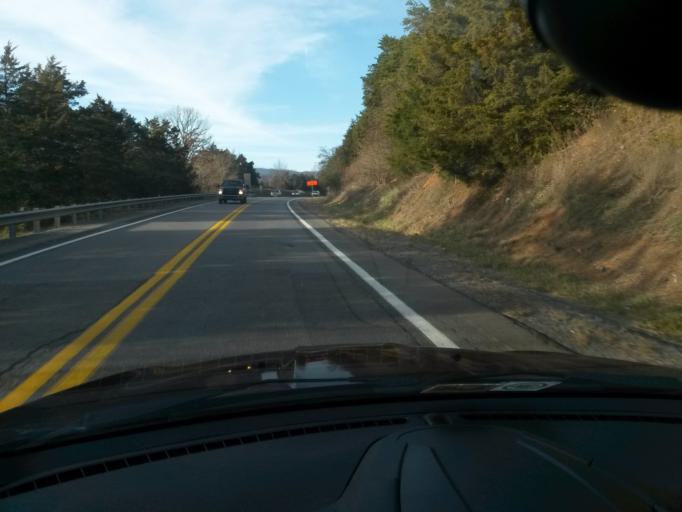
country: US
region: Virginia
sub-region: Alleghany County
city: Clifton Forge
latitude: 37.6840
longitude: -79.8076
